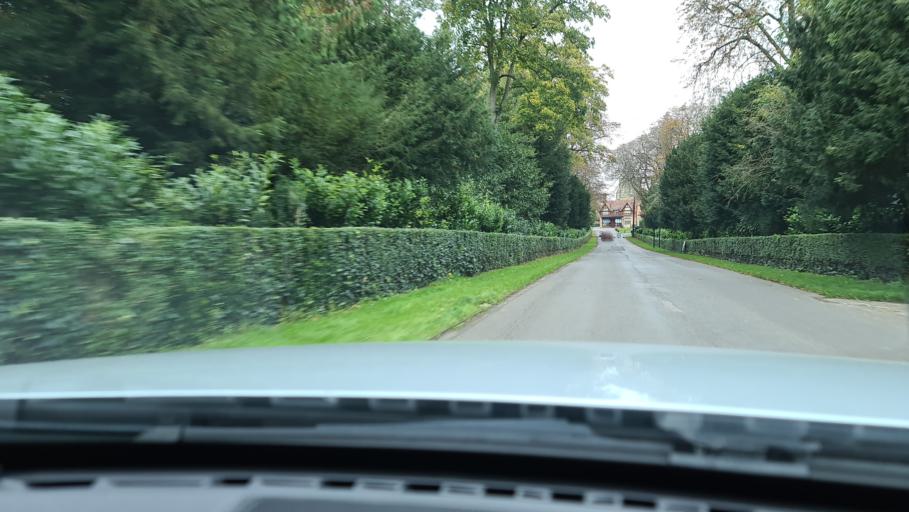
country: GB
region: England
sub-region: Buckinghamshire
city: Waddesdon
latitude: 51.8440
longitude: -0.9246
